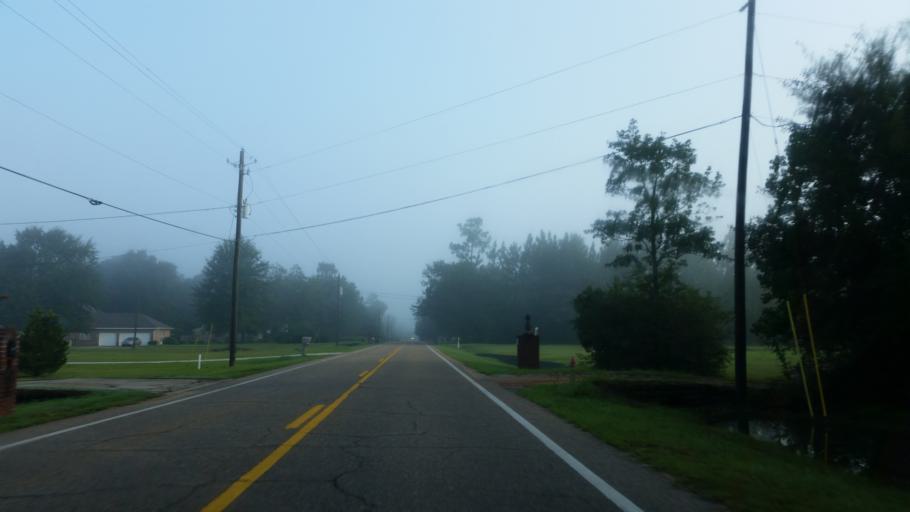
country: US
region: Florida
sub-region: Escambia County
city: Molino
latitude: 30.7292
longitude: -87.3438
